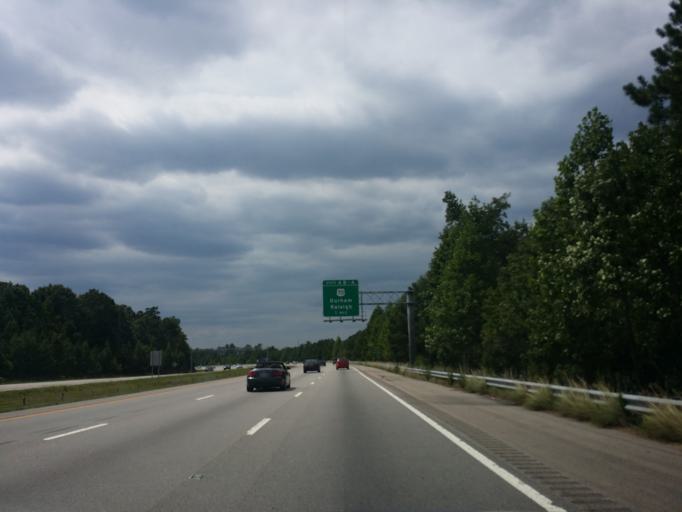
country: US
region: North Carolina
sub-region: Wake County
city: Morrisville
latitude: 35.9104
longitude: -78.7515
